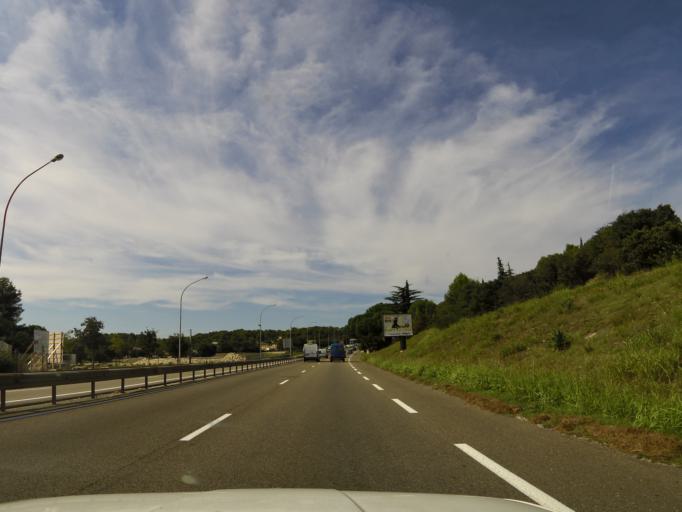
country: FR
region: Languedoc-Roussillon
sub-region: Departement du Gard
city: Nimes
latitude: 43.8257
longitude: 4.3262
